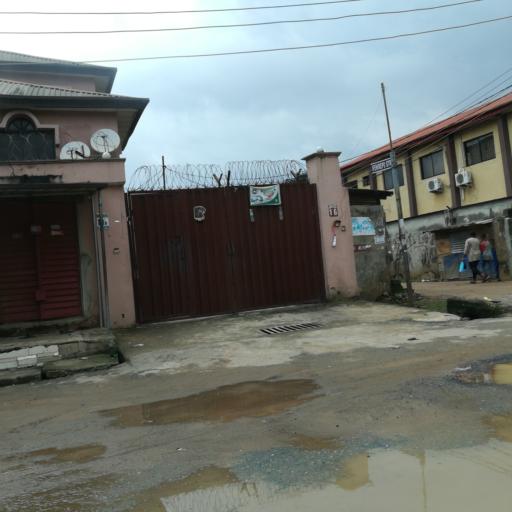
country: NG
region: Lagos
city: Agege
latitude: 6.6048
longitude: 3.3090
